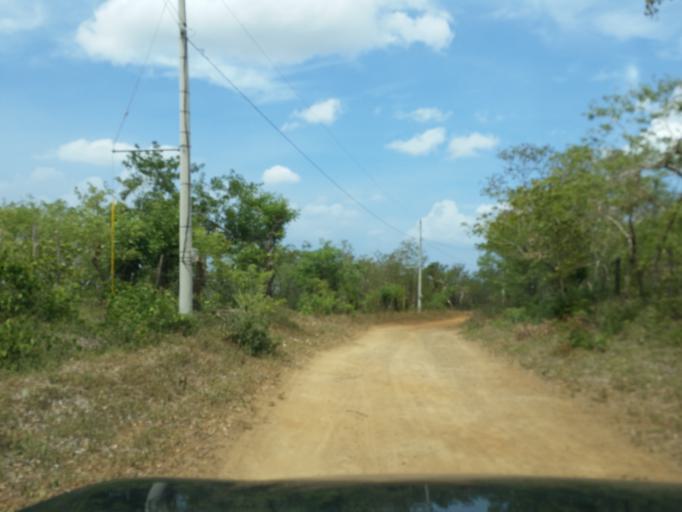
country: NI
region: Managua
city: Carlos Fonseca Amador
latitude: 11.9636
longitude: -86.4266
